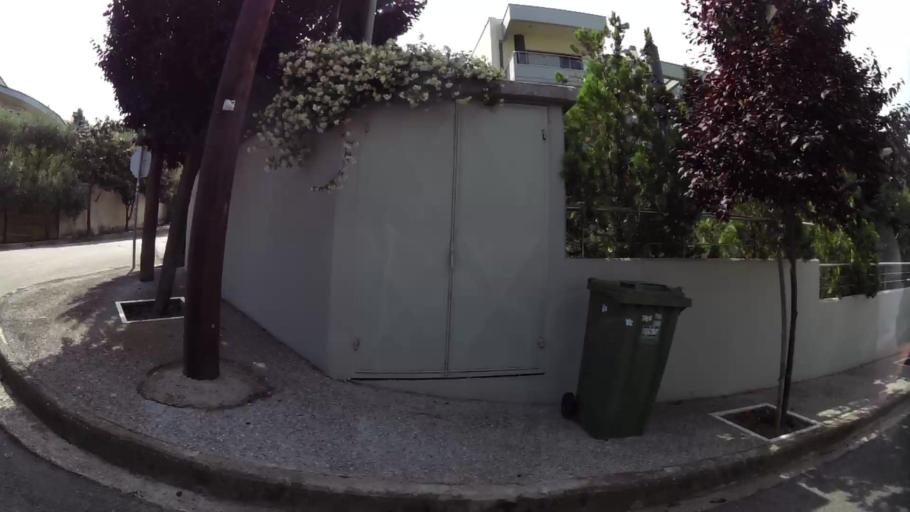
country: GR
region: Central Macedonia
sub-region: Nomos Thessalonikis
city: Panorama
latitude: 40.5803
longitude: 23.0199
